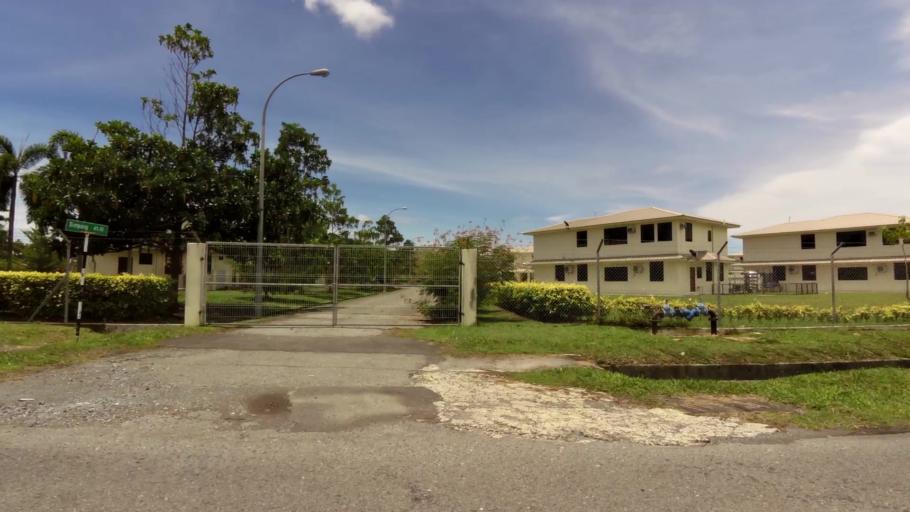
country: BN
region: Belait
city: Kuala Belait
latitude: 4.5910
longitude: 114.2500
